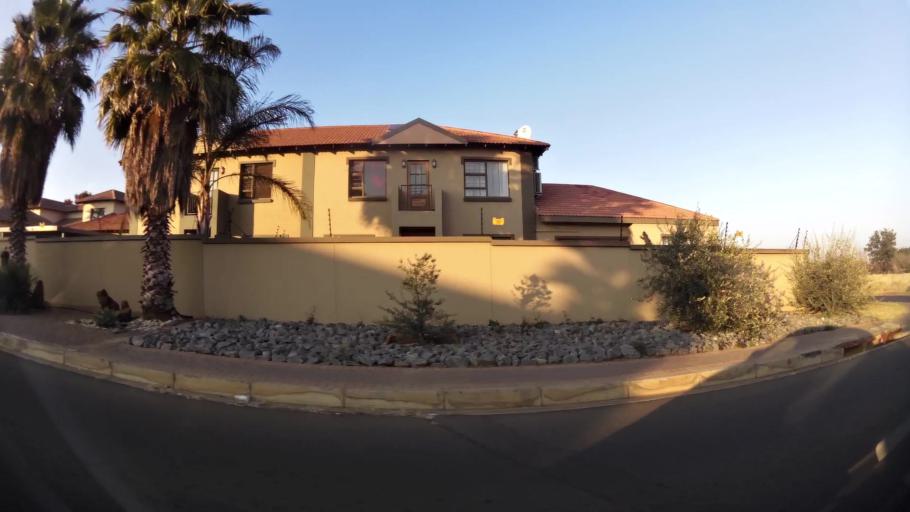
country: ZA
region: Orange Free State
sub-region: Mangaung Metropolitan Municipality
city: Bloemfontein
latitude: -29.0955
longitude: 26.1645
